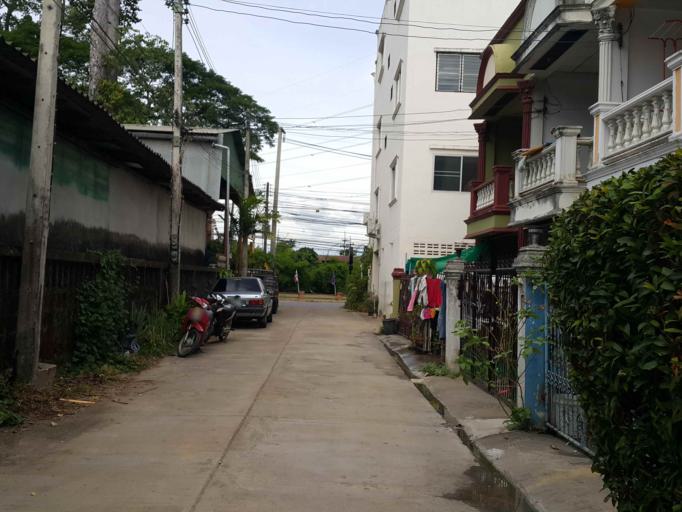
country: TH
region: Chiang Mai
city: Saraphi
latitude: 18.7497
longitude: 99.0108
